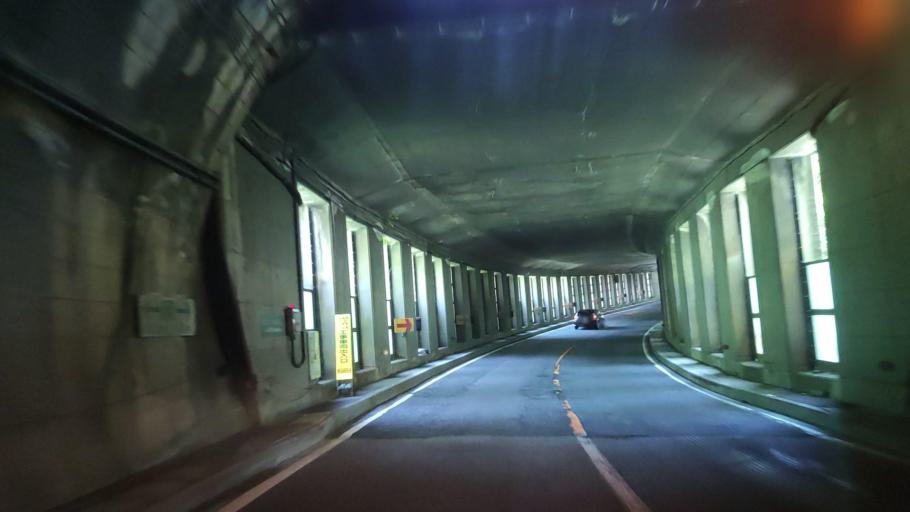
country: JP
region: Niigata
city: Itoigawa
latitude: 36.9188
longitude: 137.8737
